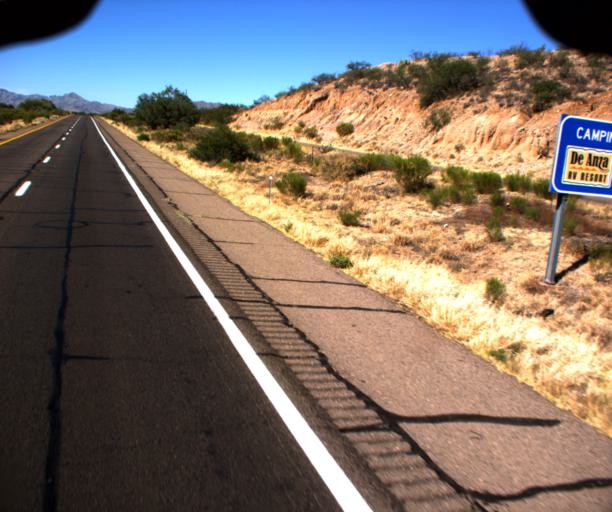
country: US
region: Arizona
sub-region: Pima County
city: Arivaca Junction
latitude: 31.7513
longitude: -111.0436
